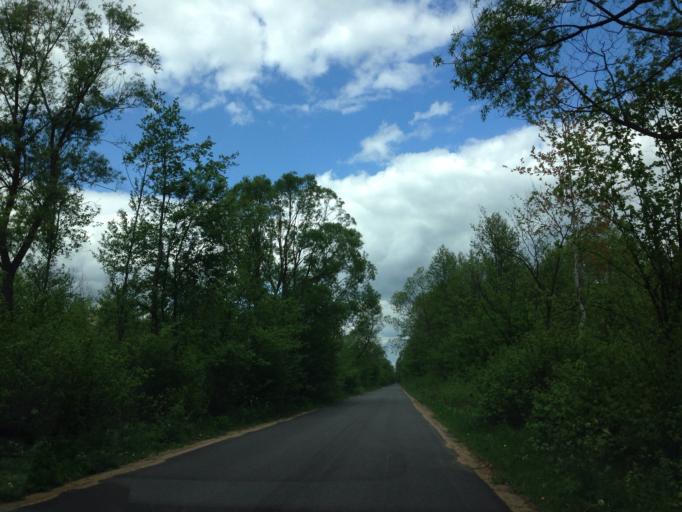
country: PL
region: Podlasie
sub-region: Powiat bialostocki
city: Tykocin
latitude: 53.3212
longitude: 22.6014
